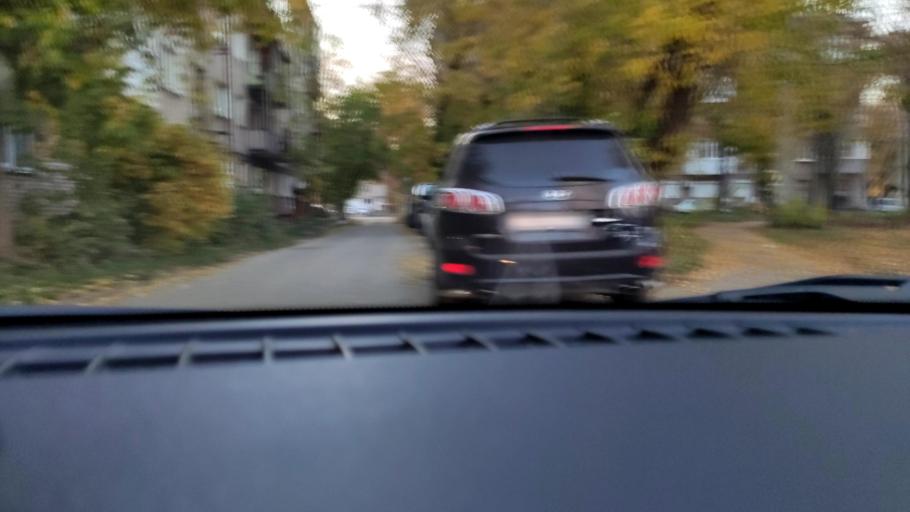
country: RU
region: Perm
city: Perm
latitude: 58.0172
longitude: 56.2885
